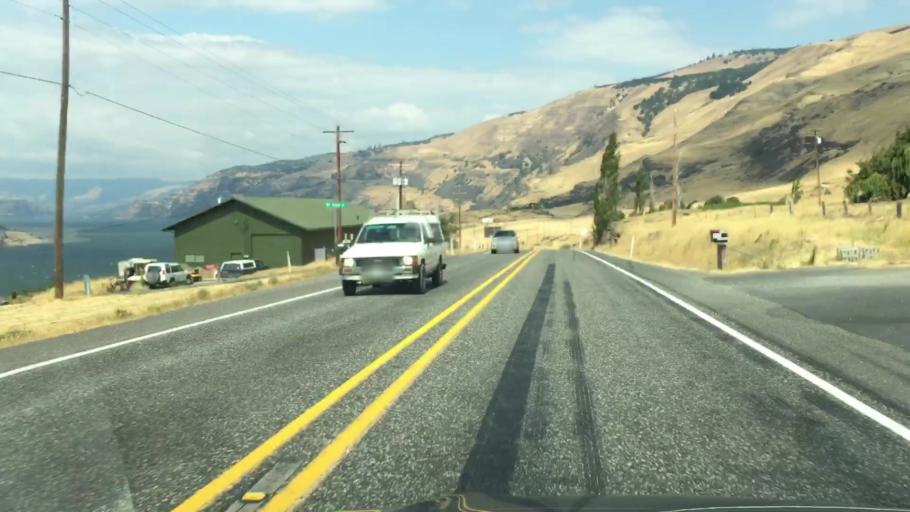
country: US
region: Washington
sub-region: Klickitat County
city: Dallesport
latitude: 45.6575
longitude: -121.1927
